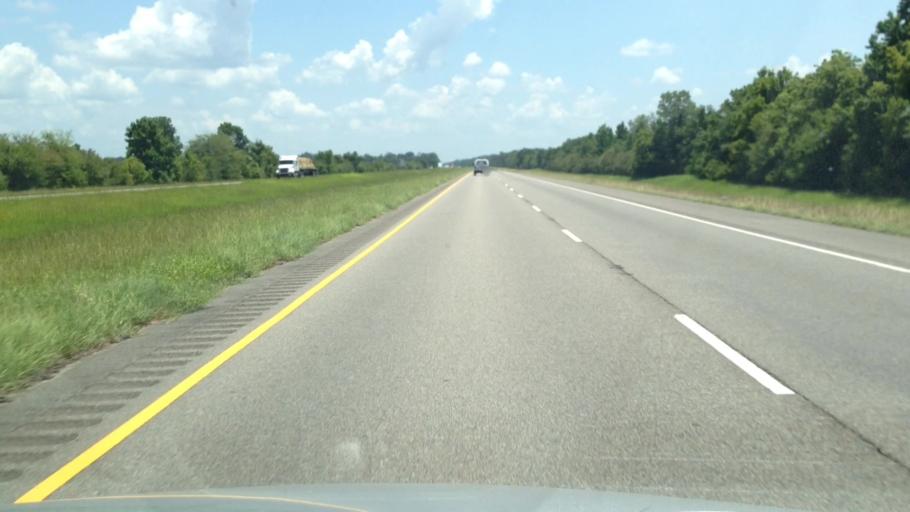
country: US
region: Louisiana
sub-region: Avoyelles Parish
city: Bunkie
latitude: 30.9379
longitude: -92.2645
